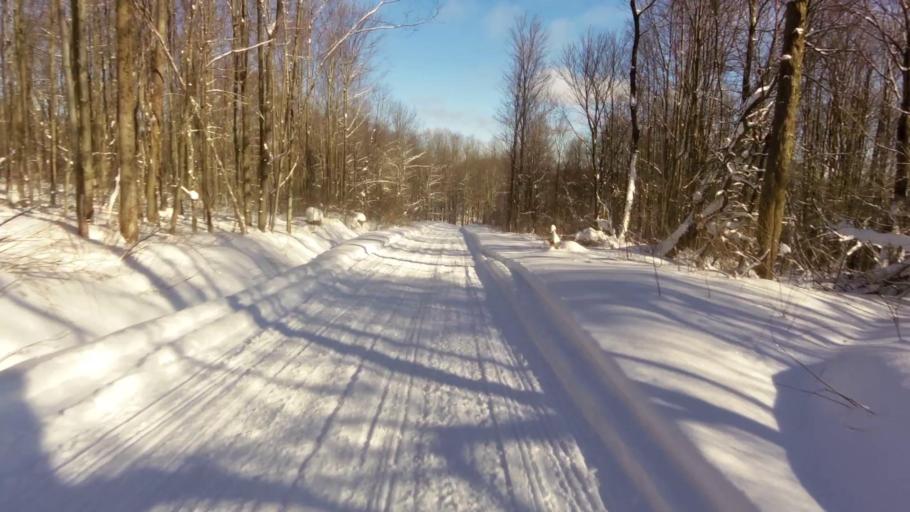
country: US
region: New York
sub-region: Chautauqua County
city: Falconer
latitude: 42.2806
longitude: -79.1281
